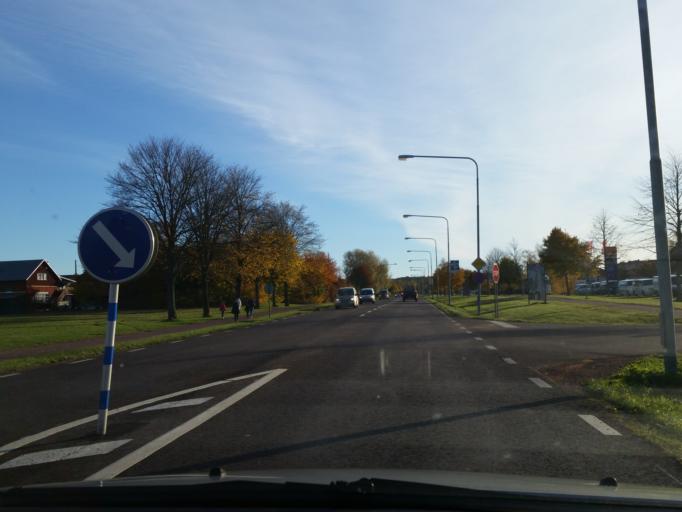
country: AX
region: Mariehamns stad
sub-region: Mariehamn
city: Mariehamn
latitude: 60.1079
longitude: 19.9438
